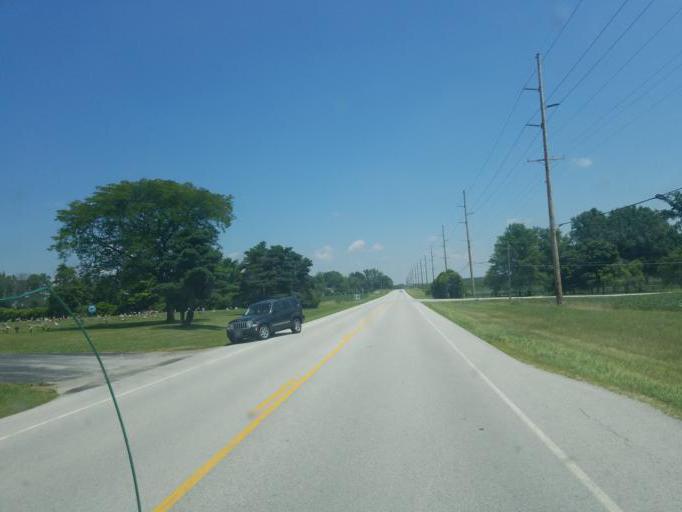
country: US
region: Ohio
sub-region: Auglaize County
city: Saint Marys
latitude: 40.5519
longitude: -84.3274
